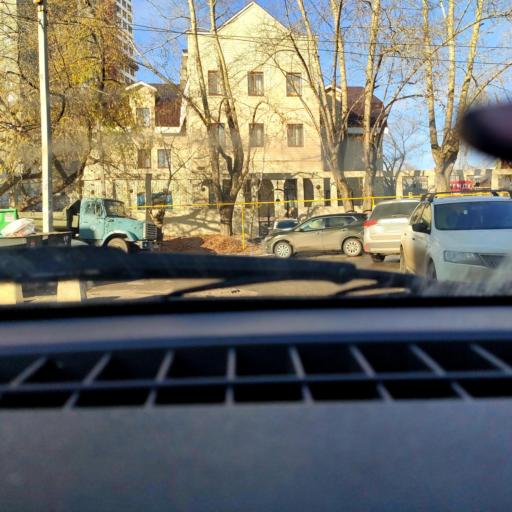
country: RU
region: Bashkortostan
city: Ufa
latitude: 54.7384
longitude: 55.9967
